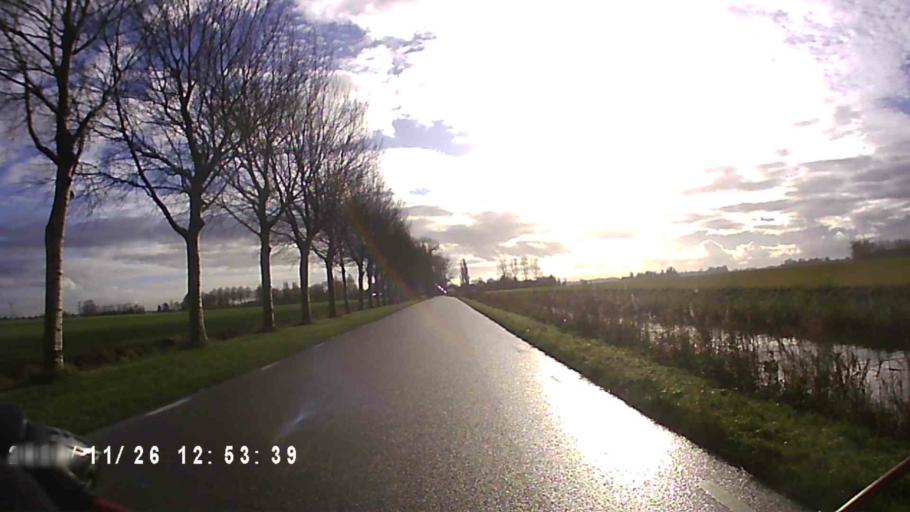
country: NL
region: Groningen
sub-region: Gemeente Appingedam
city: Appingedam
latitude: 53.3507
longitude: 6.7922
